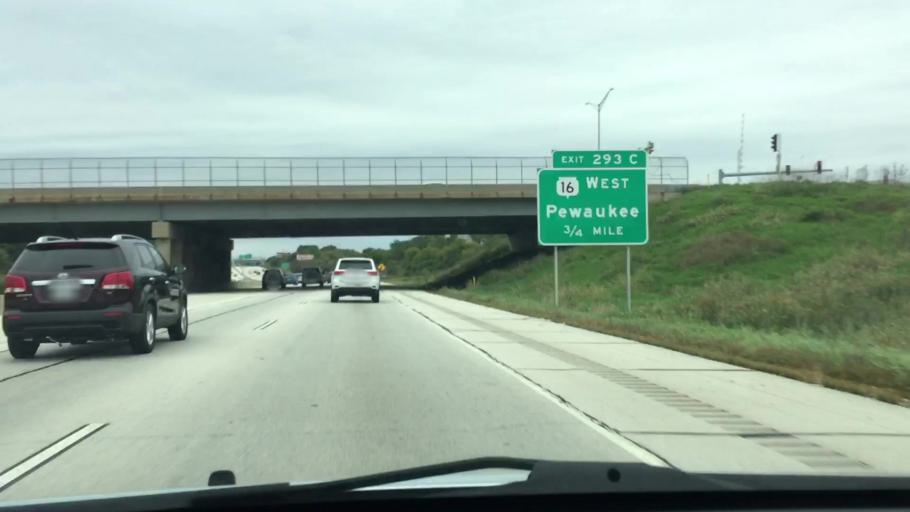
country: US
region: Wisconsin
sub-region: Waukesha County
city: Waukesha
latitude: 43.0487
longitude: -88.2187
